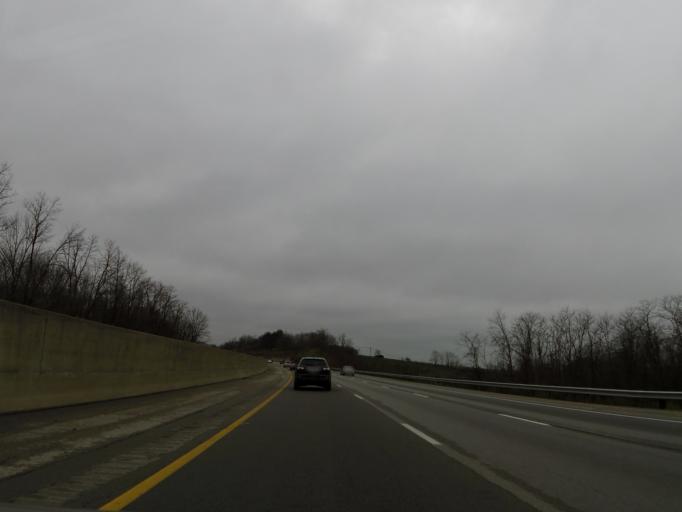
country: US
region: Kentucky
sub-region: Grant County
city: Crittenden
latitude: 38.7780
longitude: -84.6125
